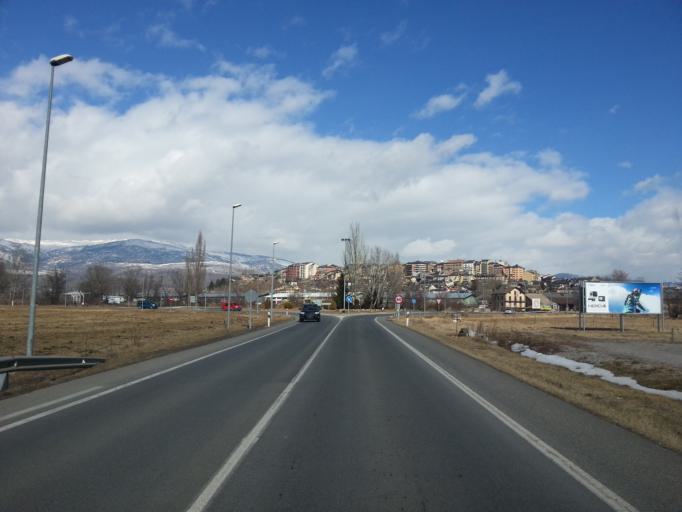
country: ES
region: Catalonia
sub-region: Provincia de Girona
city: Puigcerda
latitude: 42.4242
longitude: 1.9230
